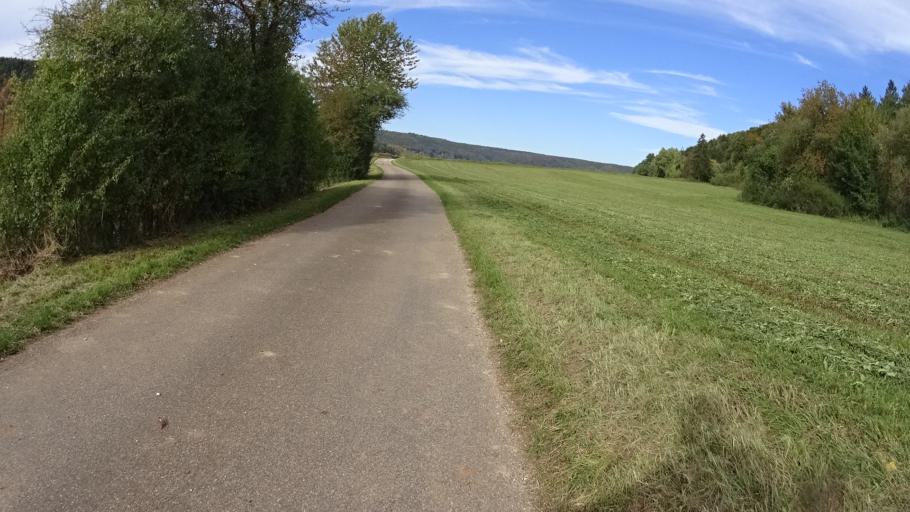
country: DE
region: Bavaria
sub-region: Upper Bavaria
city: Walting
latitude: 48.9164
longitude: 11.3062
